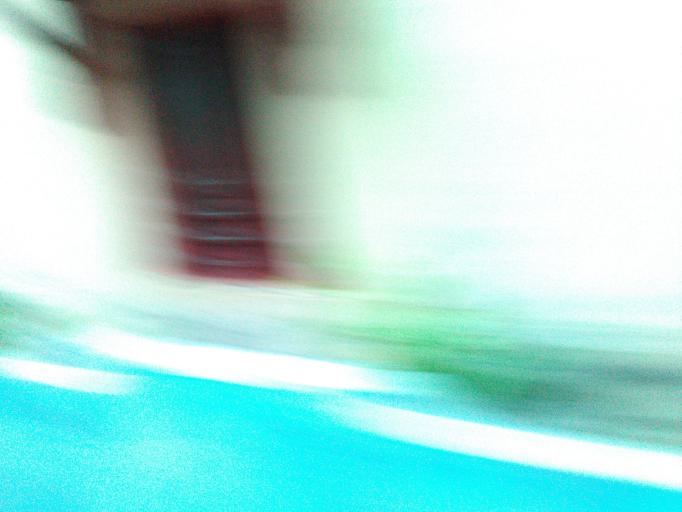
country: ID
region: Central Java
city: Ceper
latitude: -7.6617
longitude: 110.6685
